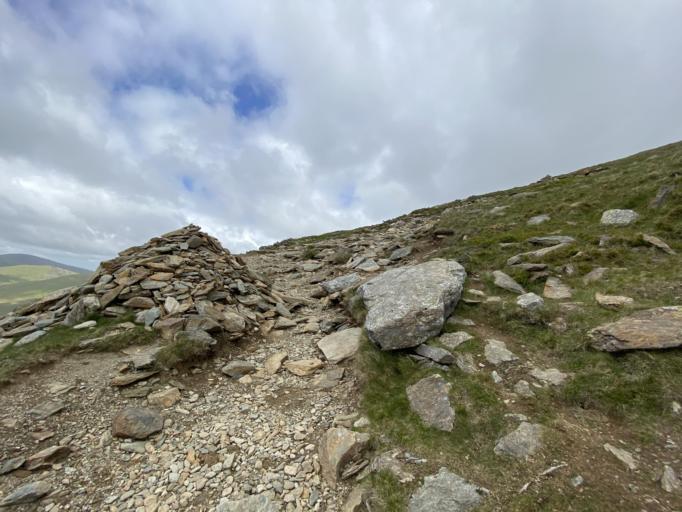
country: GB
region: Wales
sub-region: Gwynedd
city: Llanberis
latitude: 53.0619
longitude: -4.1010
